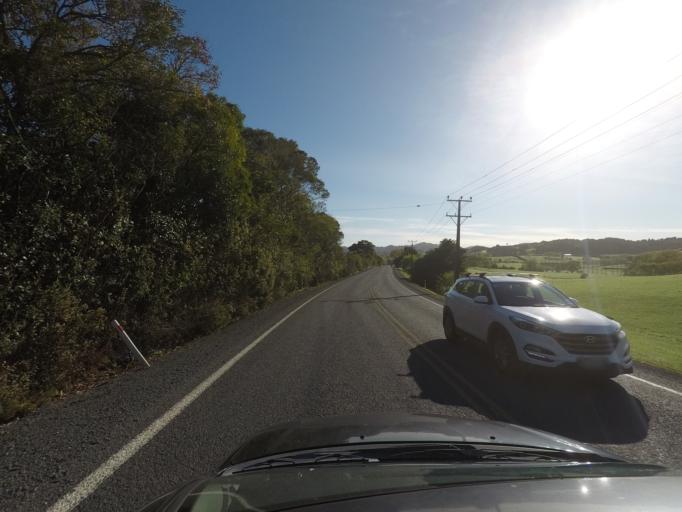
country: NZ
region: Auckland
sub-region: Auckland
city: Red Hill
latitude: -36.9923
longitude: 174.9855
